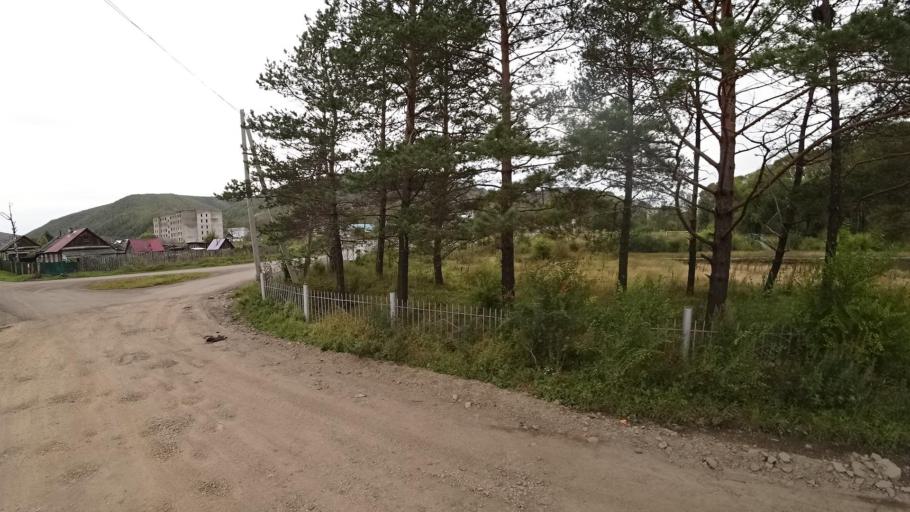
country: RU
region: Jewish Autonomous Oblast
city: Khingansk
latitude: 49.1291
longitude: 131.1980
